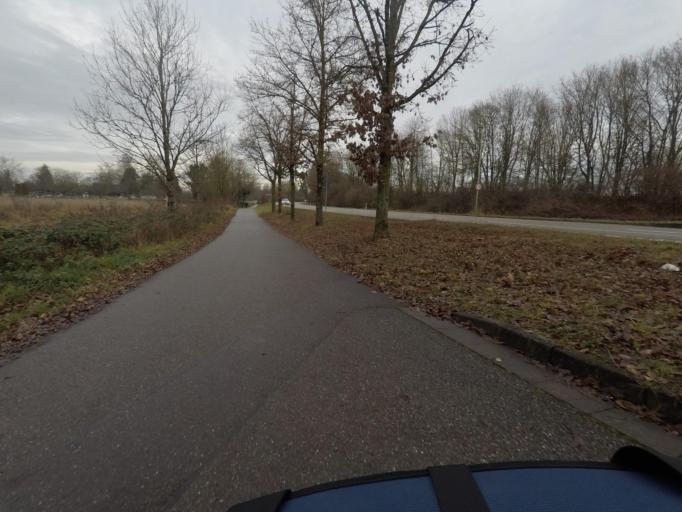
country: DE
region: Baden-Wuerttemberg
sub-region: Karlsruhe Region
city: Rheinau
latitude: 48.8734
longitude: 8.1857
